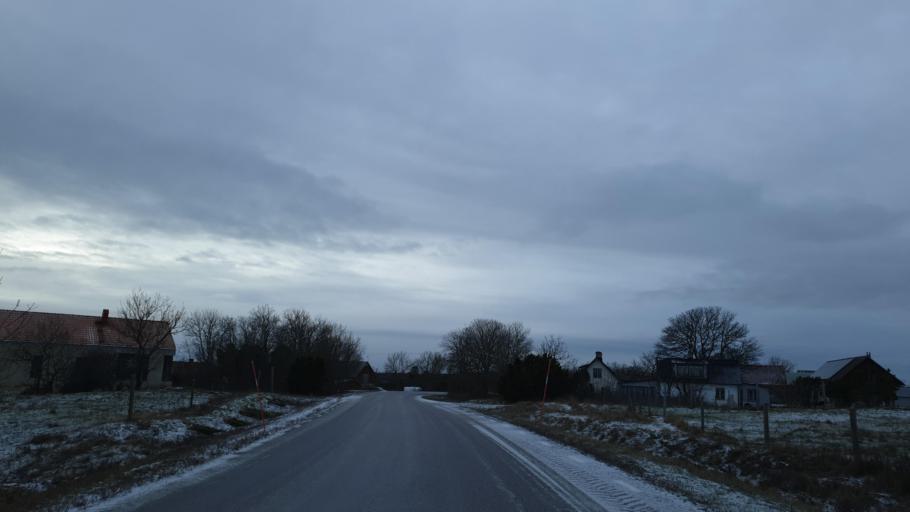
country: SE
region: Gotland
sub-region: Gotland
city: Slite
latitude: 57.4201
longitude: 18.8848
